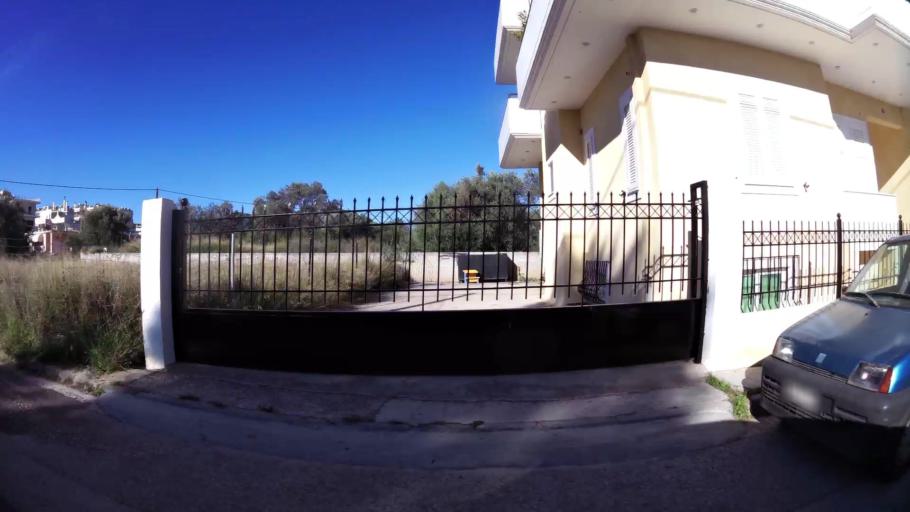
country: GR
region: Attica
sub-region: Nomarchia Anatolikis Attikis
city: Koropi
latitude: 37.9023
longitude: 23.8648
